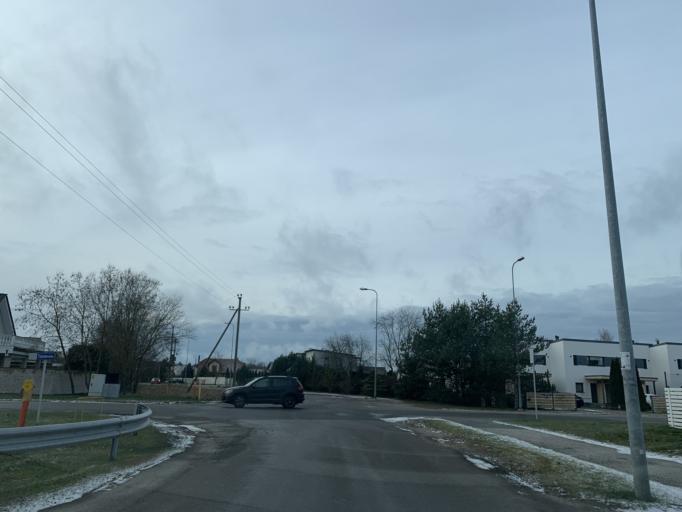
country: EE
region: Harju
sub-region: Harku vald
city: Tabasalu
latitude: 59.4387
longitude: 24.5723
